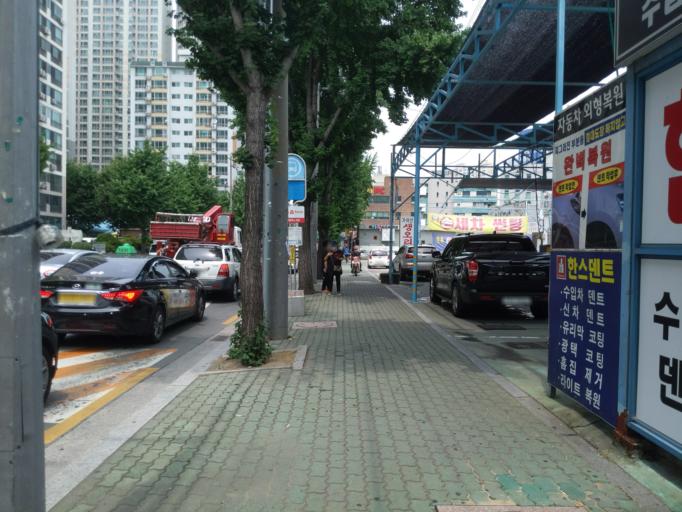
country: KR
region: Daegu
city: Hwawon
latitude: 35.8120
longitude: 128.5253
